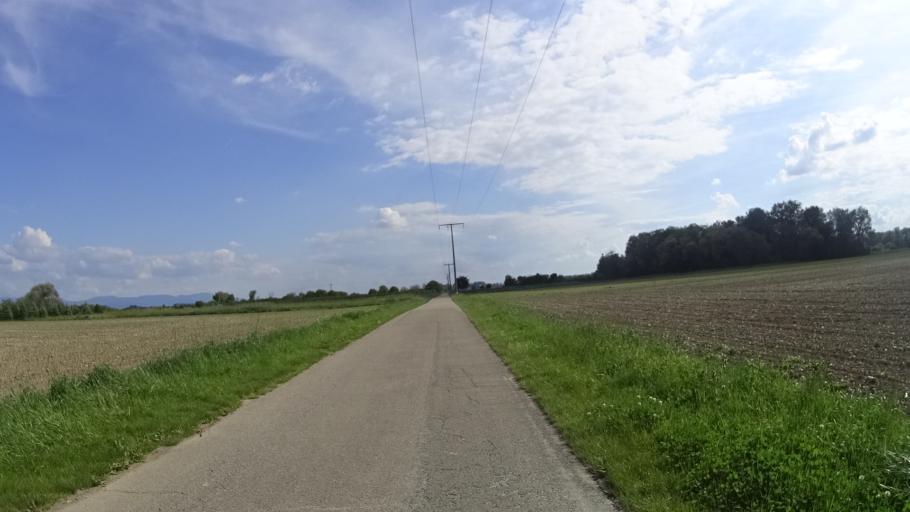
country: DE
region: Baden-Wuerttemberg
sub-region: Freiburg Region
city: Breisach am Rhein
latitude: 48.0650
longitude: 7.5899
